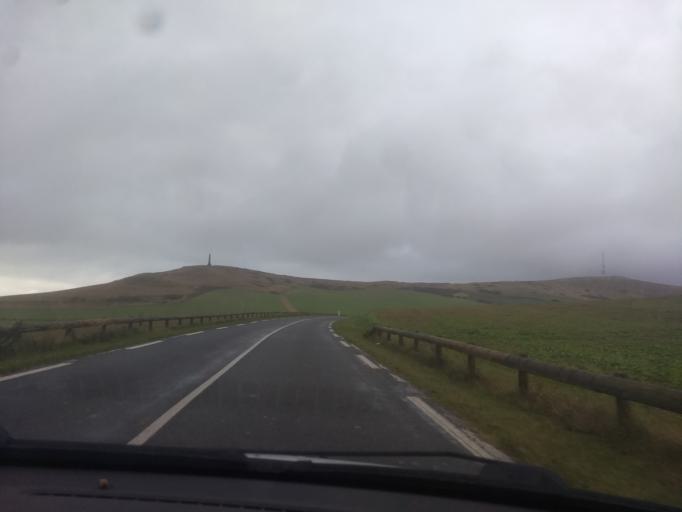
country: FR
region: Nord-Pas-de-Calais
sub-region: Departement du Pas-de-Calais
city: Wissant
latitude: 50.9154
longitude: 1.7050
